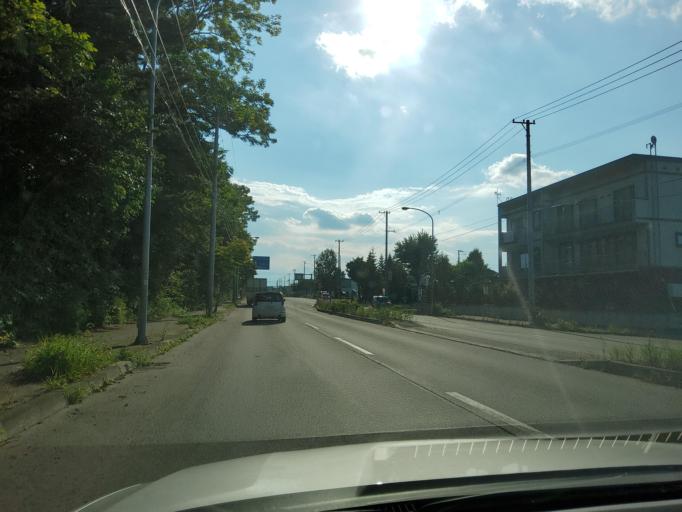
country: JP
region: Hokkaido
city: Obihiro
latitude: 42.9018
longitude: 143.2127
